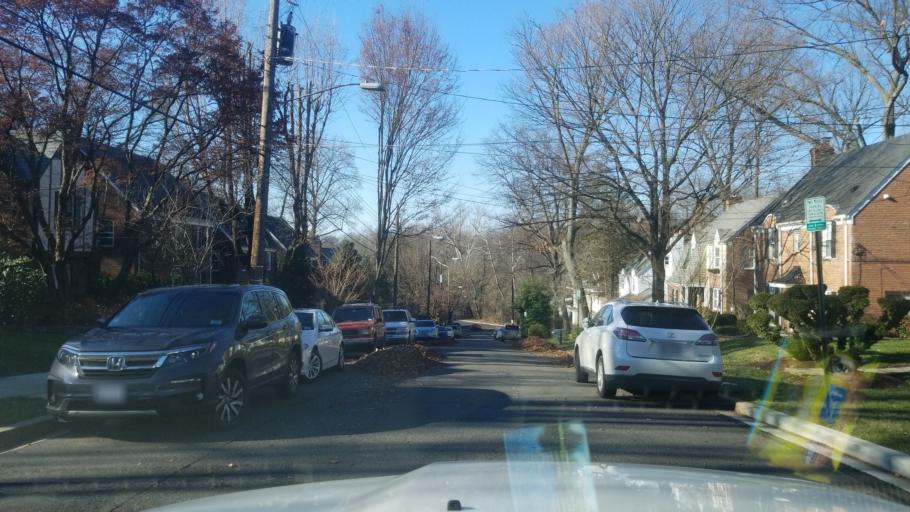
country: US
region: Maryland
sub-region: Montgomery County
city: Silver Spring
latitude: 38.9896
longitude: -77.0374
